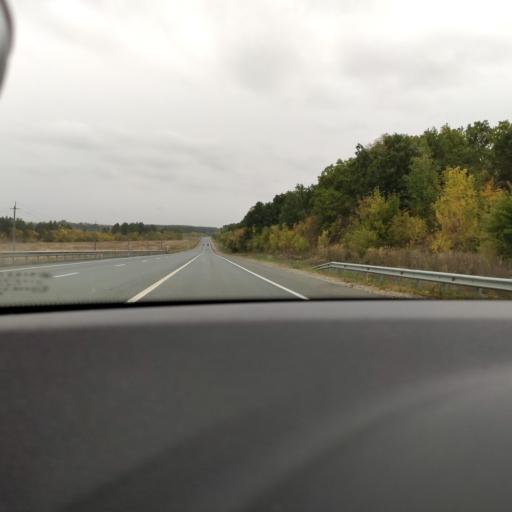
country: RU
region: Samara
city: Mirnyy
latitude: 53.5749
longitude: 50.2891
